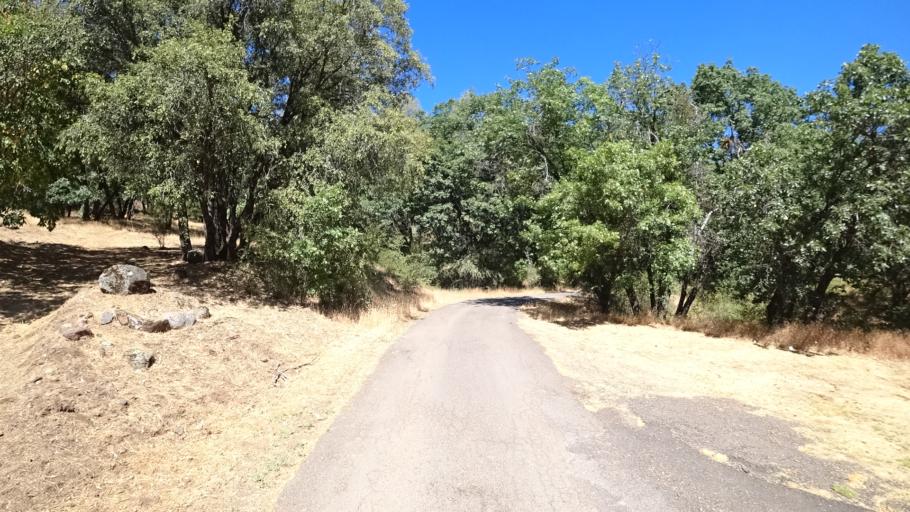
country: US
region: California
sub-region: Calaveras County
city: Forest Meadows
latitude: 38.1696
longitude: -120.3770
